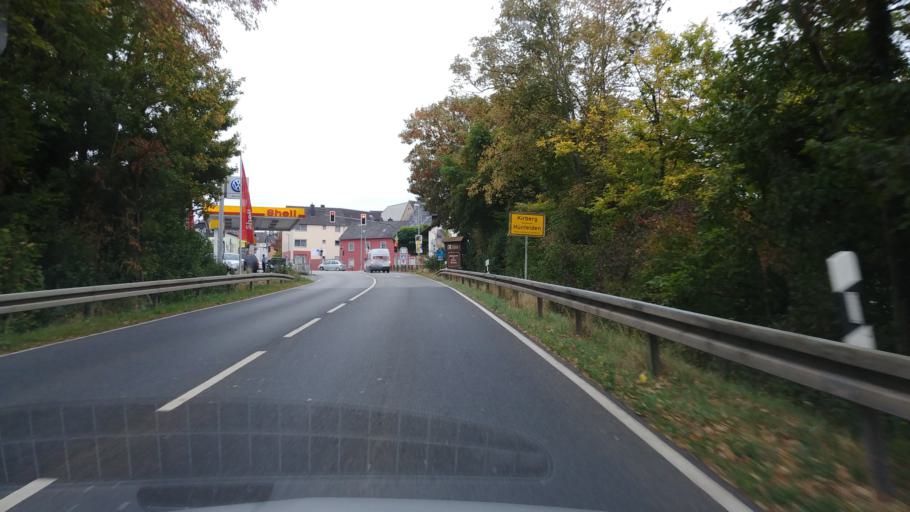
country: DE
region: Rheinland-Pfalz
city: Netzbach
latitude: 50.3101
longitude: 8.1599
